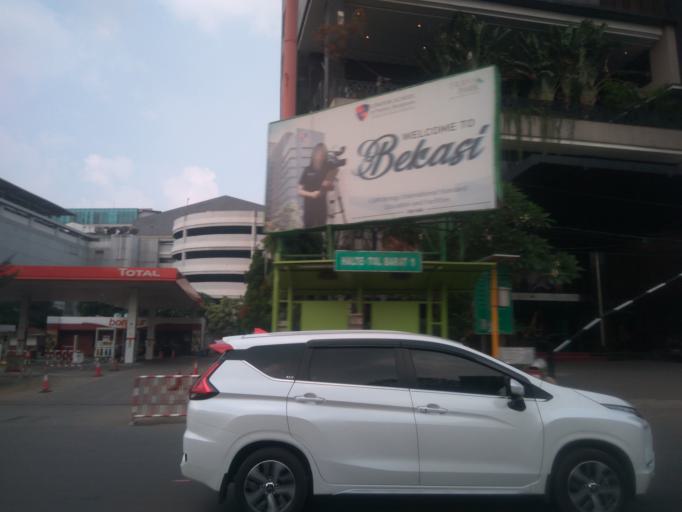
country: ID
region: West Java
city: Bekasi
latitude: -6.2503
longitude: 106.9920
